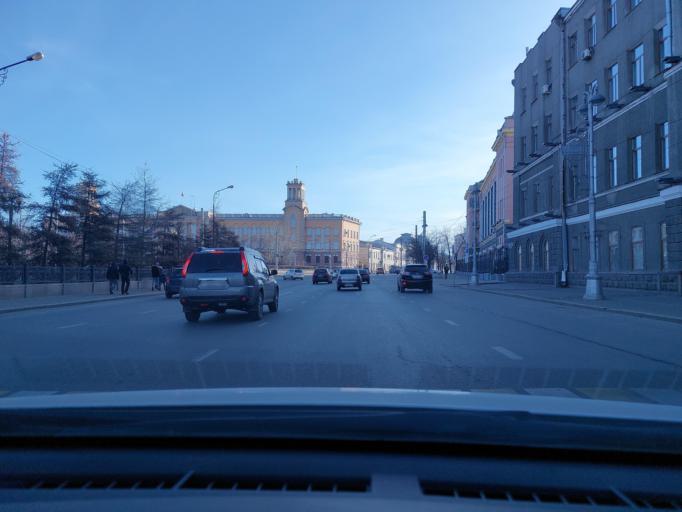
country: RU
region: Irkutsk
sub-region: Irkutskiy Rayon
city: Irkutsk
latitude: 52.2870
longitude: 104.2800
